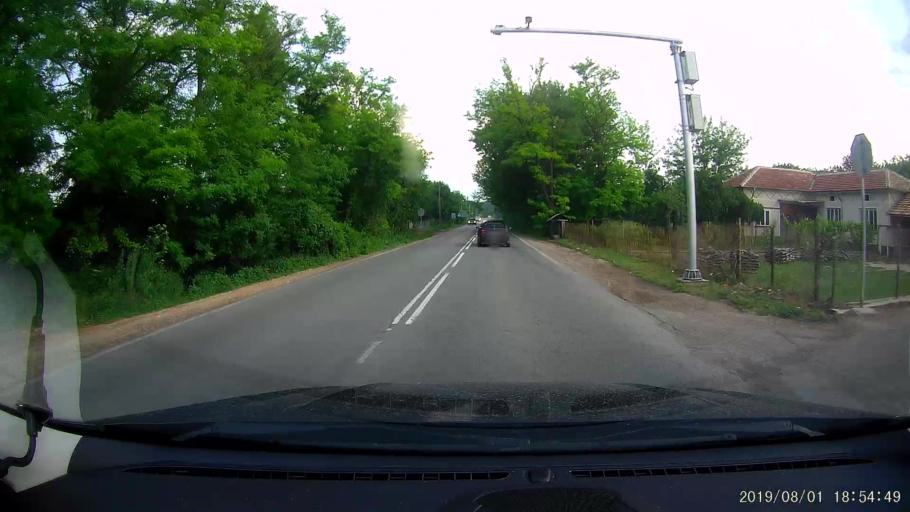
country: BG
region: Shumen
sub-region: Obshtina Shumen
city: Shumen
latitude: 43.1905
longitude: 27.0032
